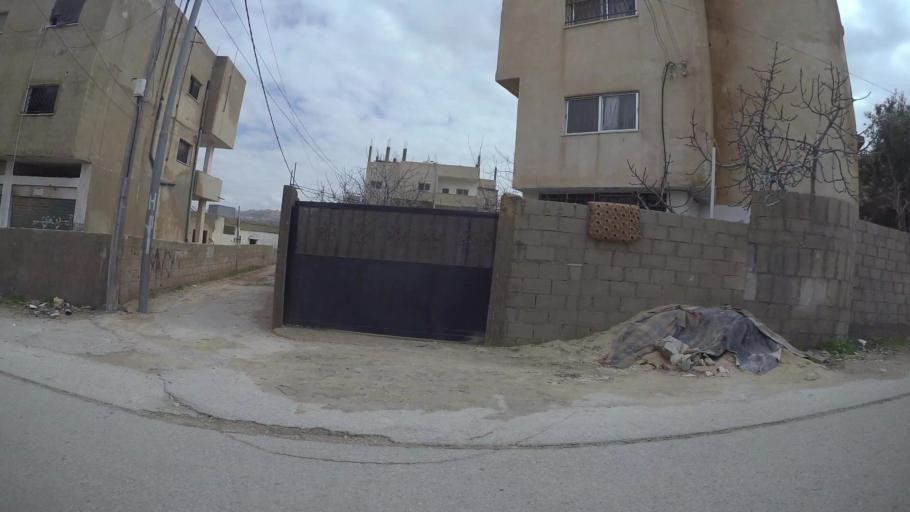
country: JO
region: Amman
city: Al Jubayhah
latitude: 32.0504
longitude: 35.8301
